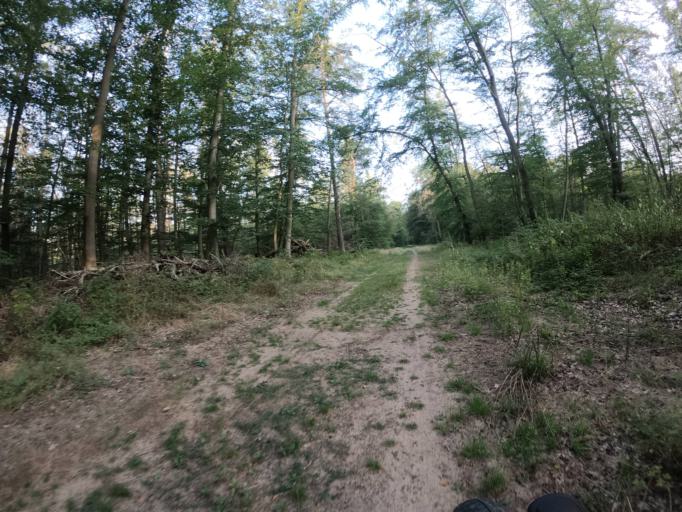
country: DE
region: Hesse
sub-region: Regierungsbezirk Darmstadt
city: Nauheim
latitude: 49.9777
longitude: 8.4996
